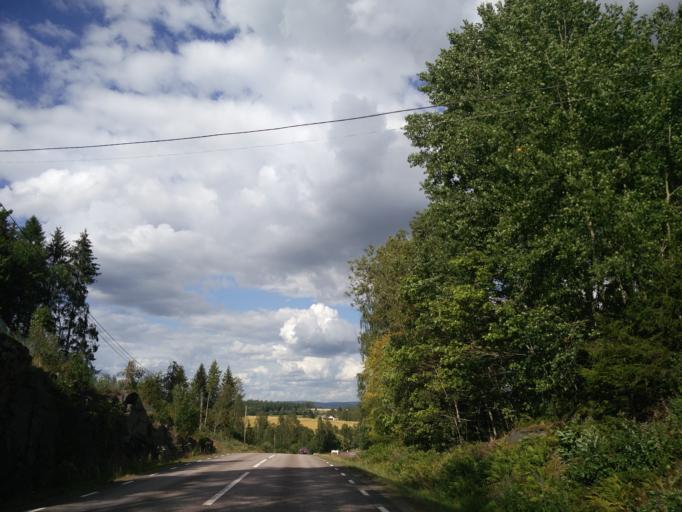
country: SE
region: Vaermland
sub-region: Sunne Kommun
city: Sunne
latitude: 59.7194
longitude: 13.1118
